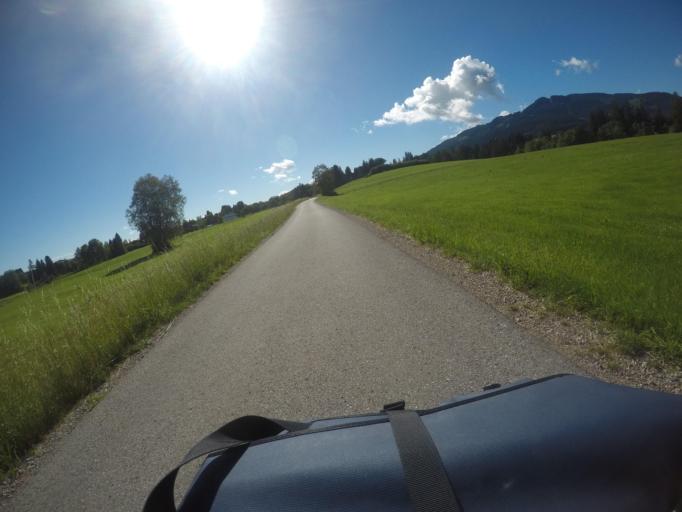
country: DE
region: Bavaria
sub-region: Swabia
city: Oy-Mittelberg
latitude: 47.6282
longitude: 10.4677
